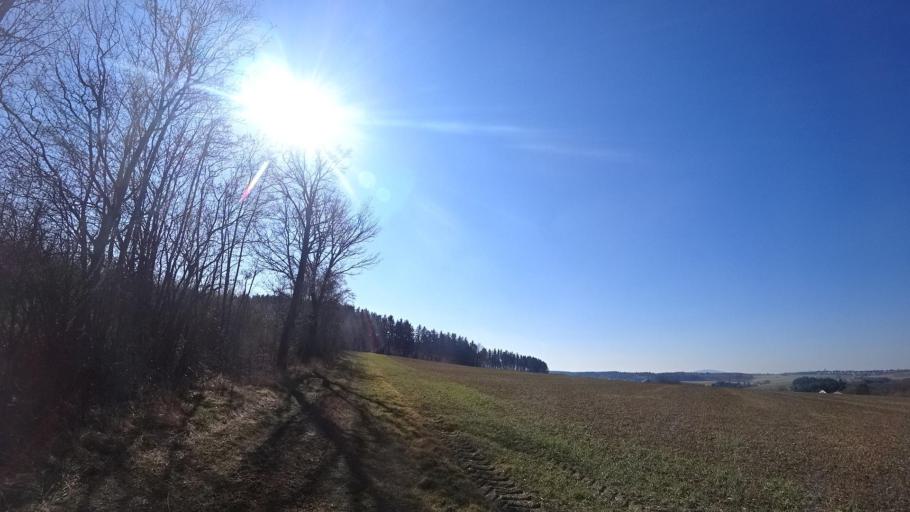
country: DE
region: Rheinland-Pfalz
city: Schonborn
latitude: 49.9605
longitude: 7.4663
